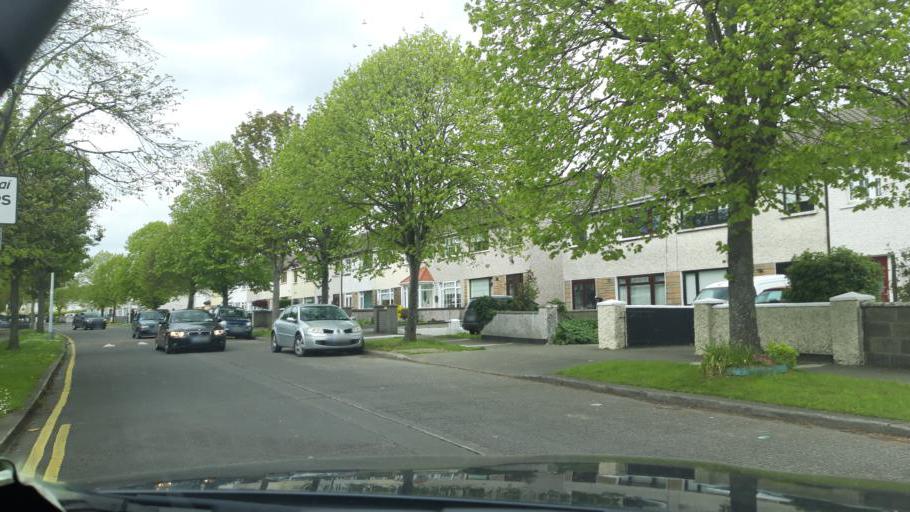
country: IE
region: Leinster
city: Donaghmede
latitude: 53.3931
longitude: -6.1559
